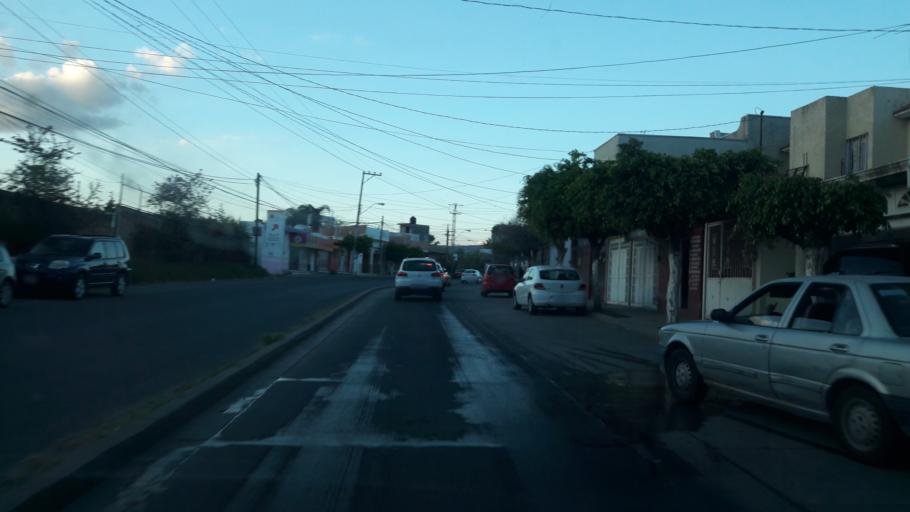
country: MX
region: Guanajuato
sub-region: Leon
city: Medina
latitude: 21.1579
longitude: -101.6348
